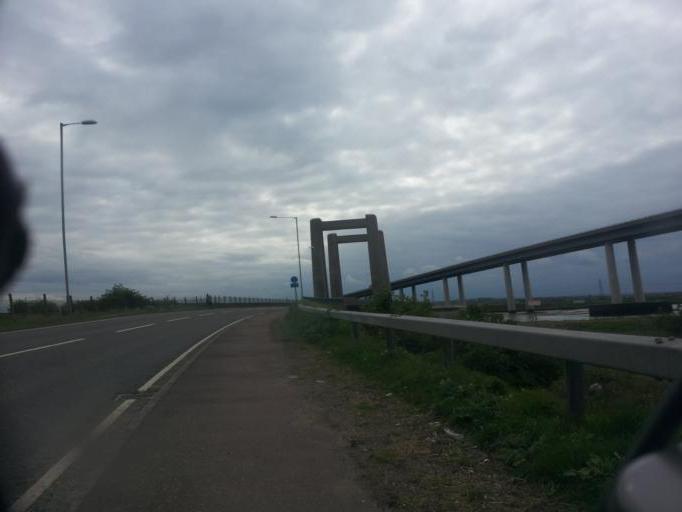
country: GB
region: England
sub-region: Kent
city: Queenborough
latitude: 51.3918
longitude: 0.7525
